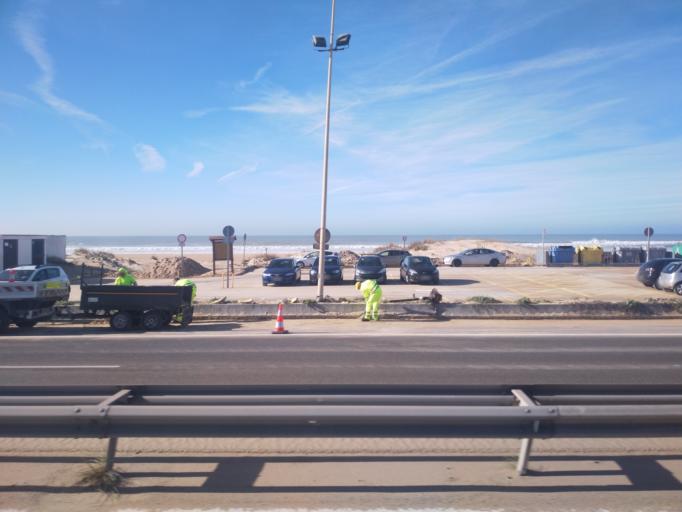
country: ES
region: Andalusia
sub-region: Provincia de Cadiz
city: Cadiz
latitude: 36.4809
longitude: -6.2624
